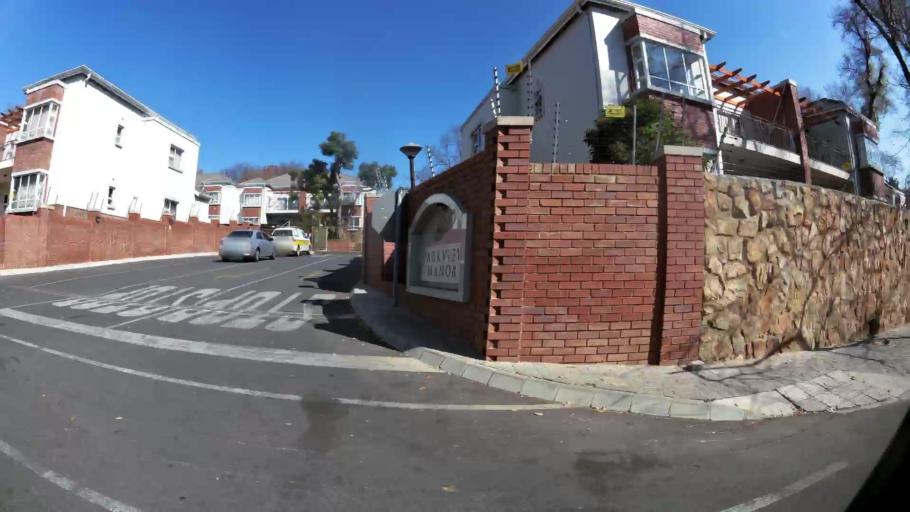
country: ZA
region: Gauteng
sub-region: City of Johannesburg Metropolitan Municipality
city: Johannesburg
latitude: -26.1648
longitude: 28.0329
